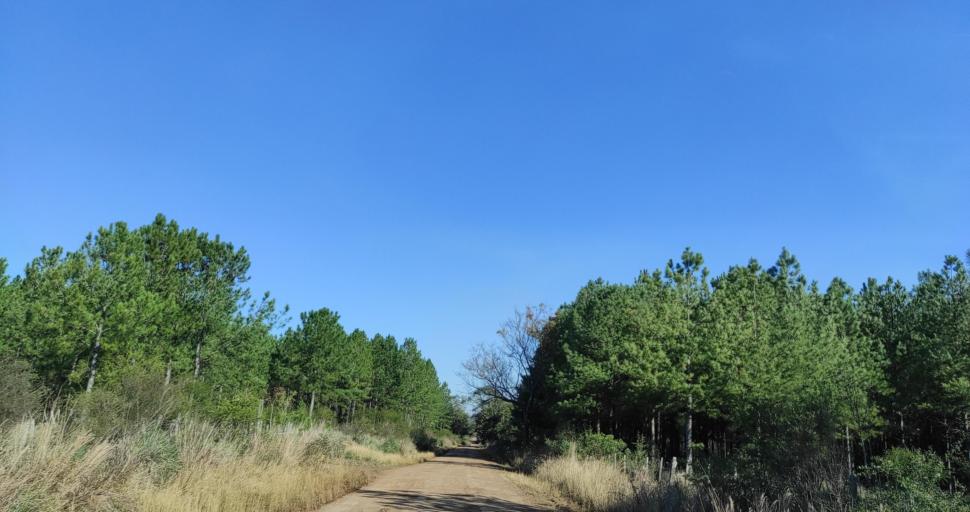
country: AR
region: Misiones
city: Cerro Cora
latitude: -27.6515
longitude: -55.6579
